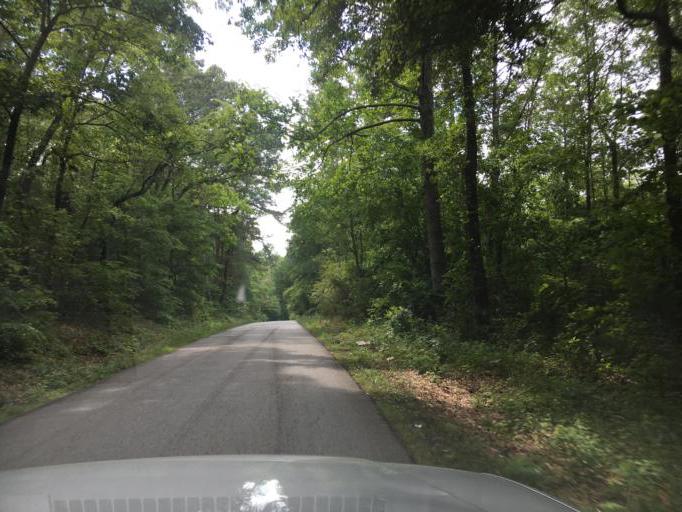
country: US
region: South Carolina
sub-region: Spartanburg County
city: Fairforest
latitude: 34.9050
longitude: -82.0332
